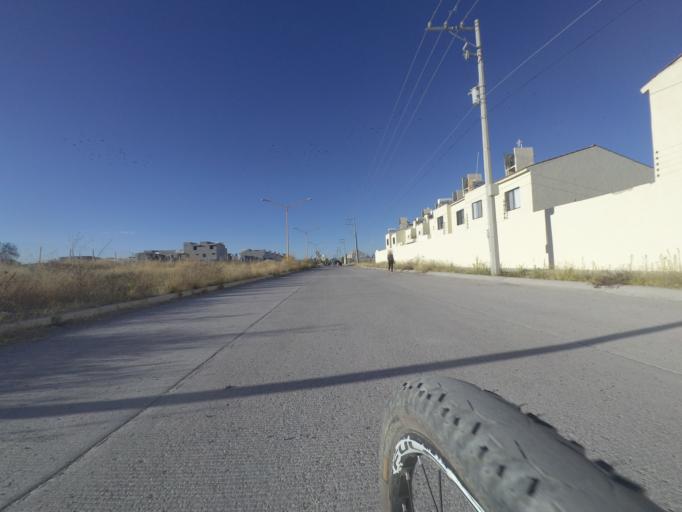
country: MX
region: Aguascalientes
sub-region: Aguascalientes
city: La Loma de los Negritos
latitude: 21.8516
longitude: -102.3461
